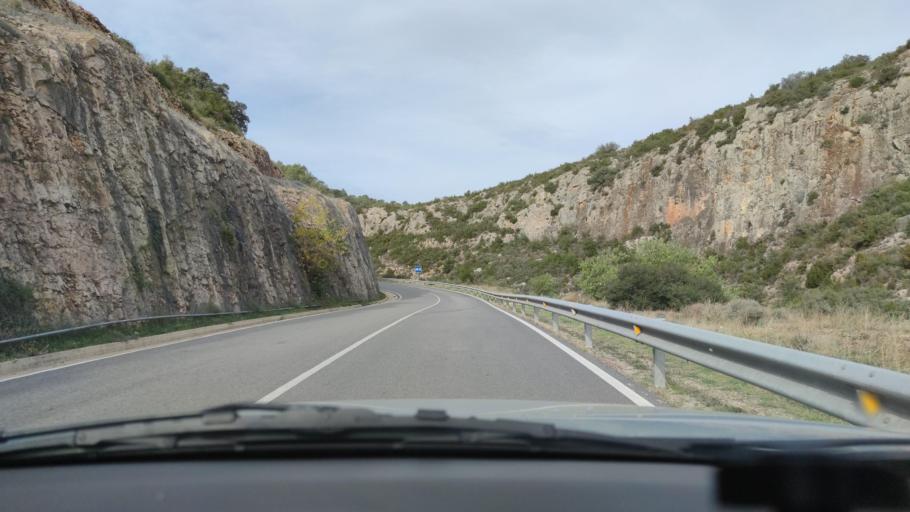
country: ES
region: Catalonia
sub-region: Provincia de Lleida
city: Artesa de Segre
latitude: 41.9323
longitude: 1.0542
